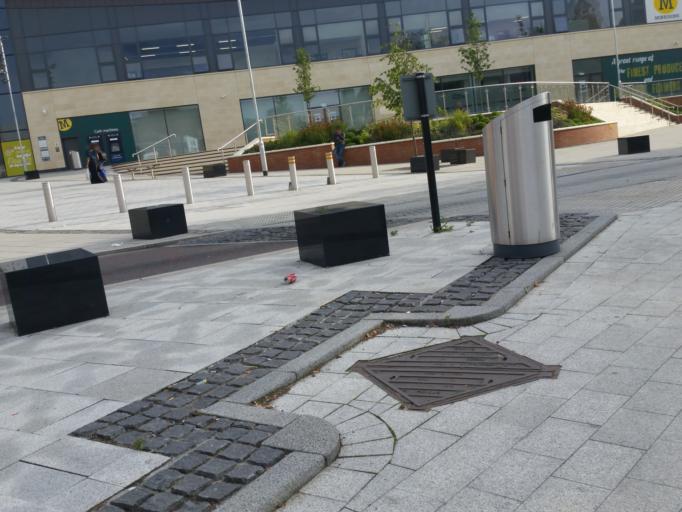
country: GB
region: England
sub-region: Borough of Swindon
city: Swindon
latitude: 51.5583
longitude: -1.7809
